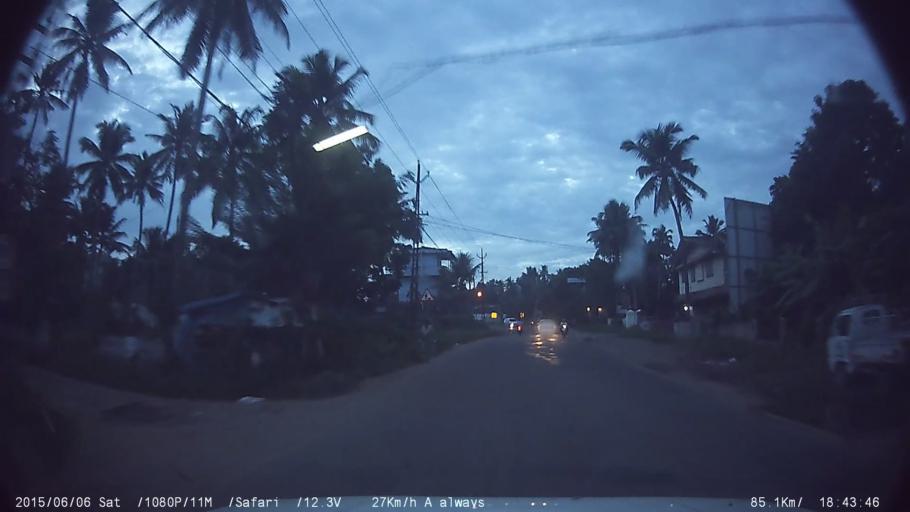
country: IN
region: Kerala
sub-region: Pattanamtitta
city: Tiruvalla
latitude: 9.4015
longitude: 76.5631
